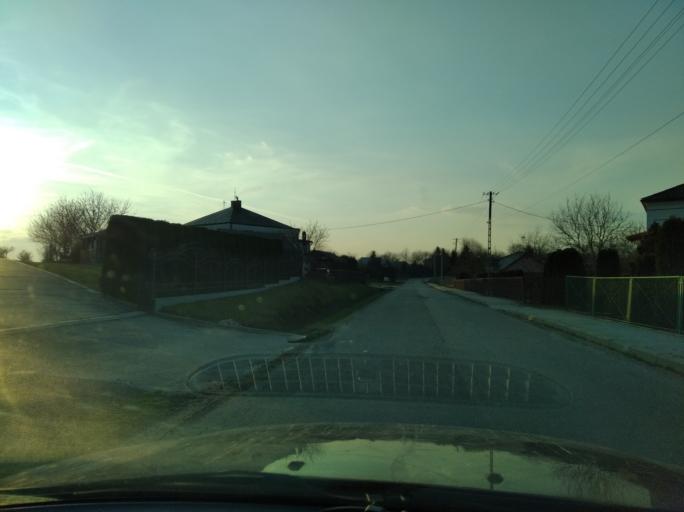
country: PL
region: Subcarpathian Voivodeship
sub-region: Powiat przeworski
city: Zarzecze
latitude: 49.9679
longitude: 22.5553
